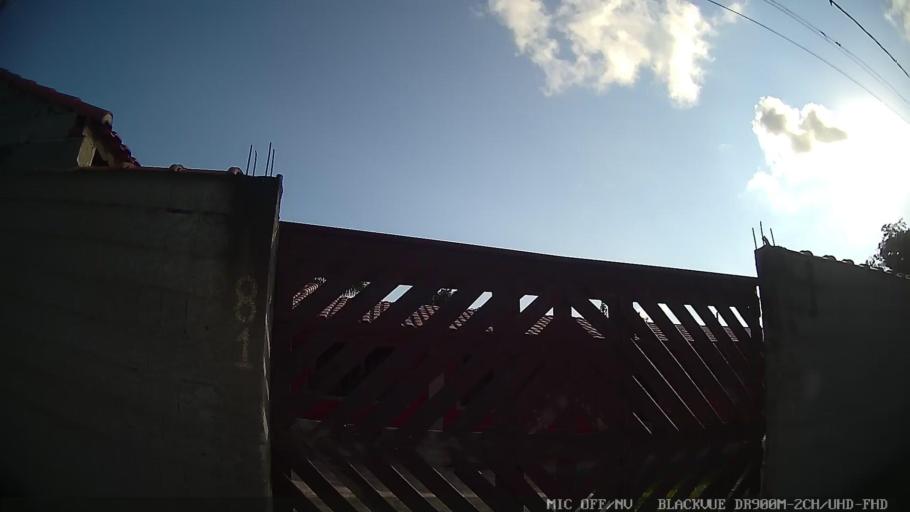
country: BR
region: Sao Paulo
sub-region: Itanhaem
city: Itanhaem
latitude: -24.1767
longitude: -46.8227
